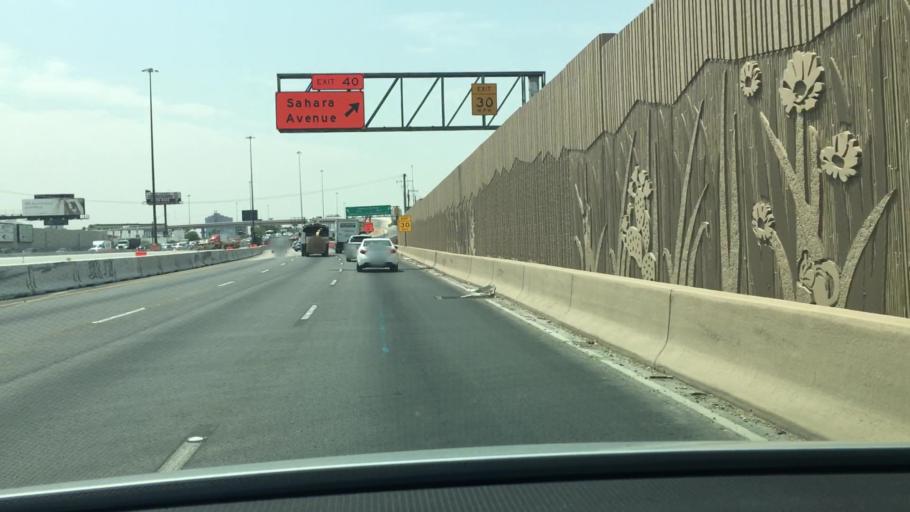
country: US
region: Nevada
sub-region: Clark County
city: Las Vegas
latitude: 36.1471
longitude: -115.1693
